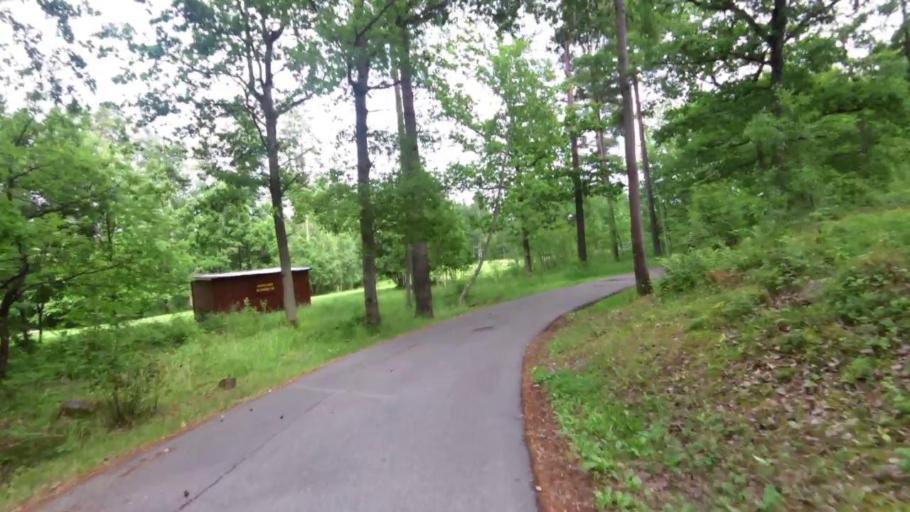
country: SE
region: OEstergoetland
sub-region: Linkopings Kommun
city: Linkoping
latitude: 58.4130
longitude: 15.5781
